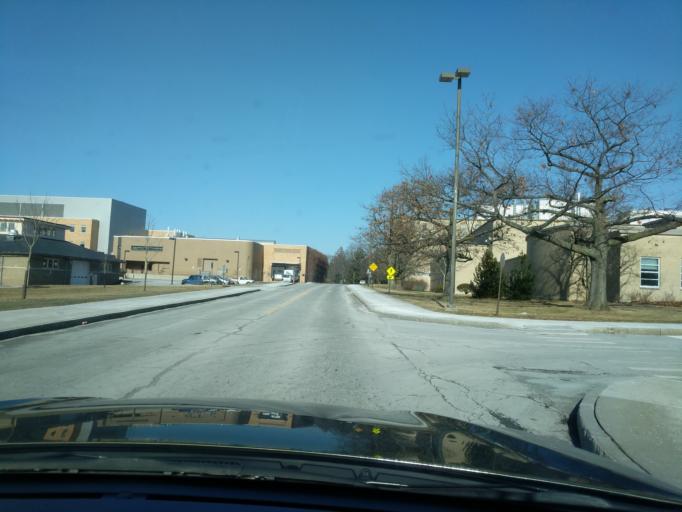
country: US
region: New York
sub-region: Tompkins County
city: East Ithaca
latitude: 42.4459
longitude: -76.4697
